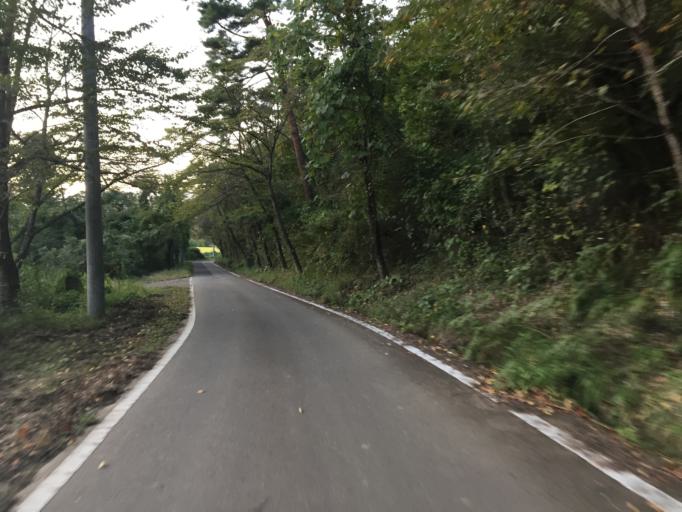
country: JP
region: Fukushima
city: Yanagawamachi-saiwaicho
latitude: 37.8527
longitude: 140.6311
